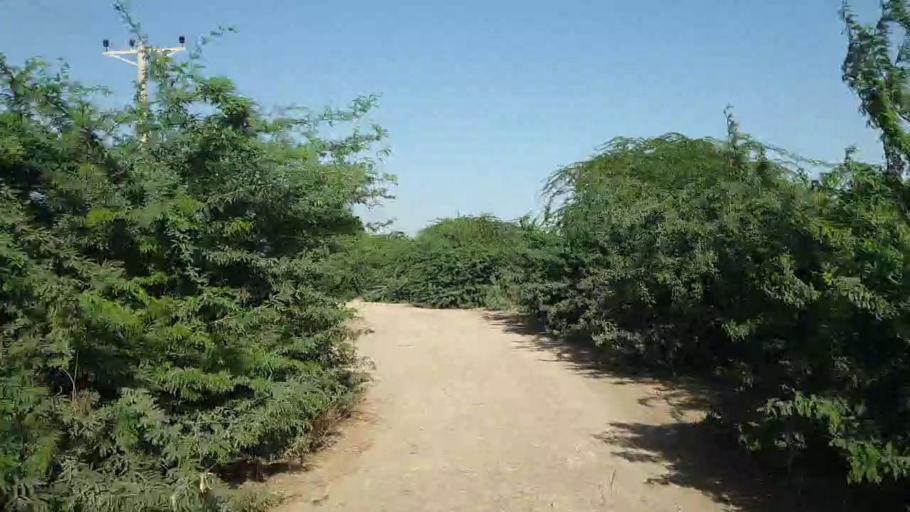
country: PK
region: Sindh
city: Badin
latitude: 24.6028
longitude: 68.9188
